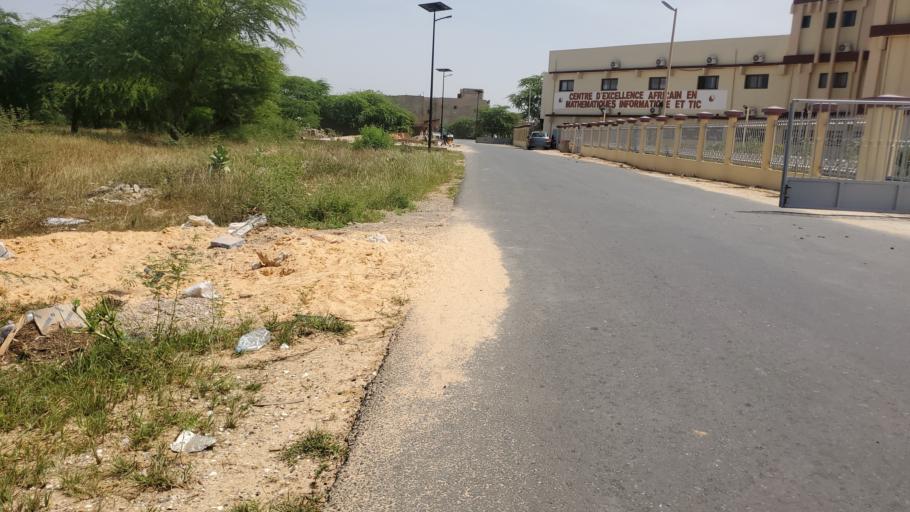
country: SN
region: Saint-Louis
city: Saint-Louis
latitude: 16.0566
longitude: -16.4268
